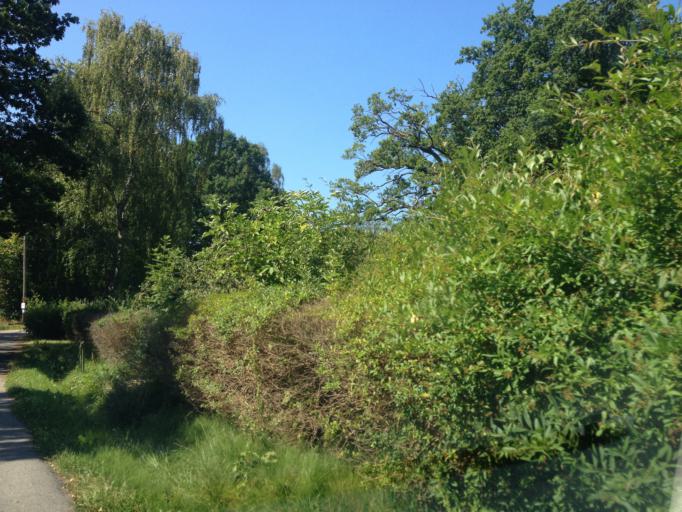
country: SE
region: Vaestra Goetaland
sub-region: Alingsas Kommun
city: Ingared
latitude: 57.8500
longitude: 12.4526
